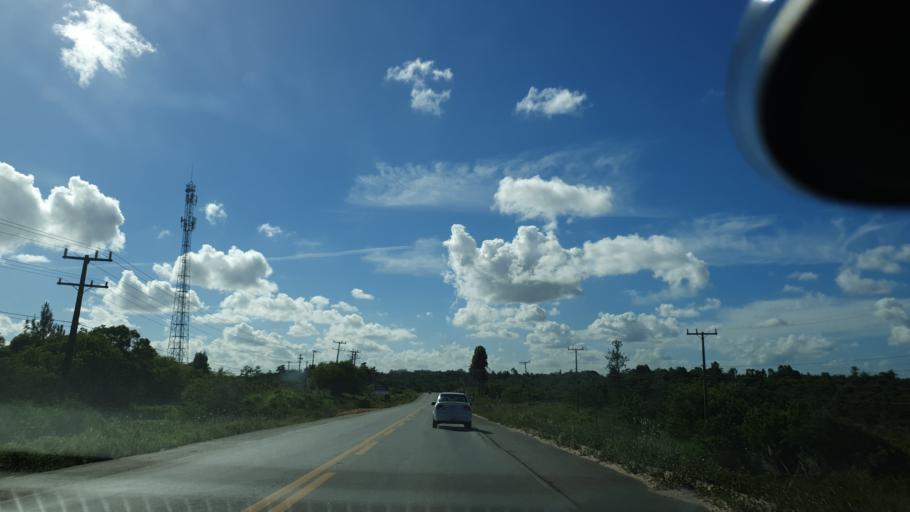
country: BR
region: Bahia
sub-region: Camacari
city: Camacari
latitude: -12.6846
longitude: -38.2751
